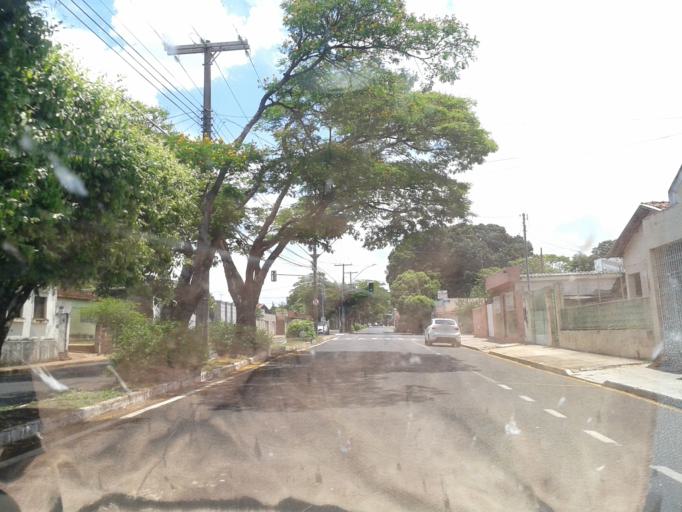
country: BR
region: Minas Gerais
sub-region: Uberaba
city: Uberaba
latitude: -19.7436
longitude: -47.9505
